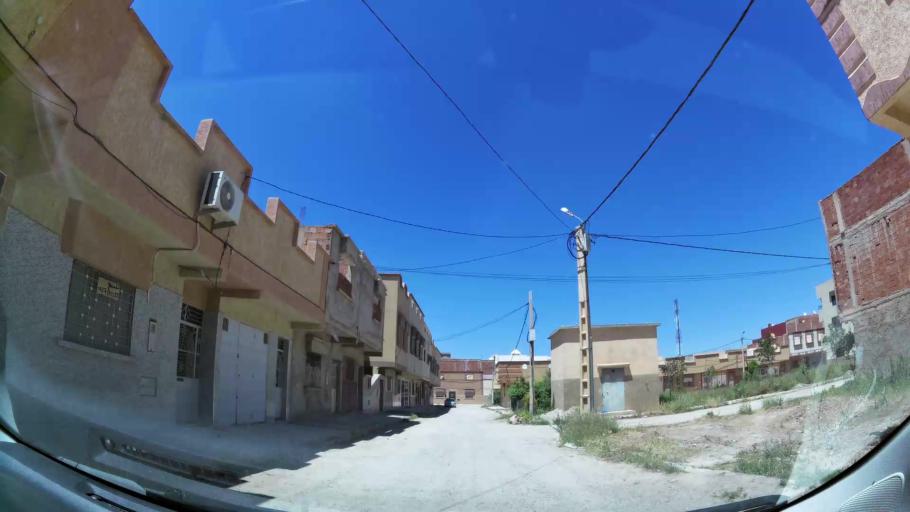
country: MA
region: Oriental
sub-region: Oujda-Angad
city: Oujda
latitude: 34.6771
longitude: -1.8553
